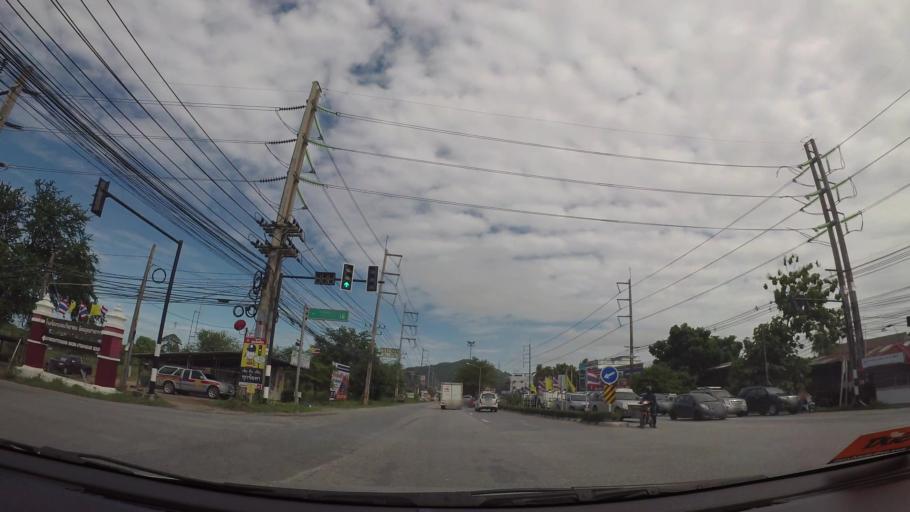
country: TH
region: Rayong
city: Ban Chang
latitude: 12.7402
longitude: 101.1221
